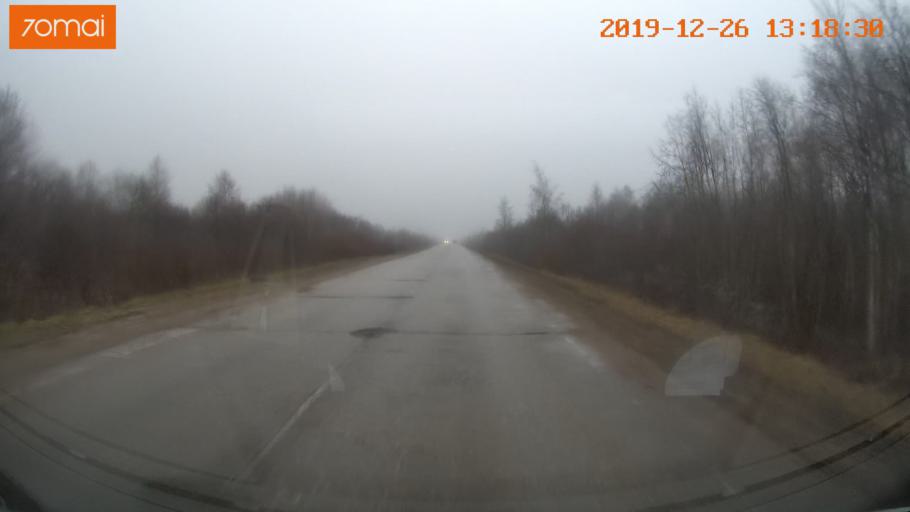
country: RU
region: Vologda
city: Cherepovets
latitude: 58.9542
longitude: 38.1229
